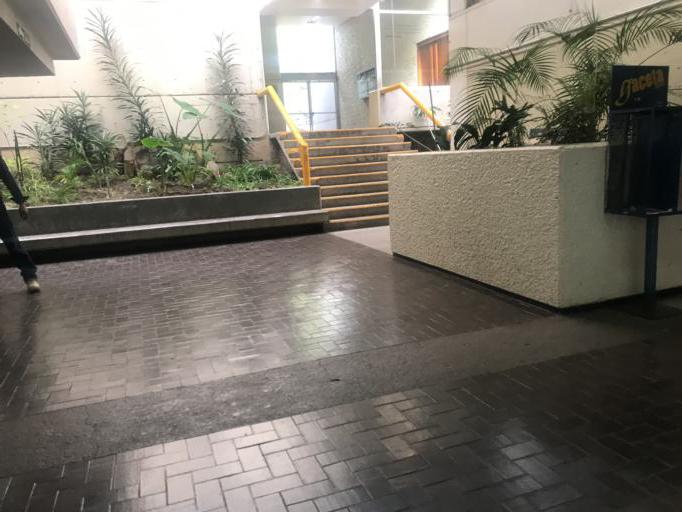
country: MX
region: Mexico City
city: Tlalpan
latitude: 19.3190
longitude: -99.1783
